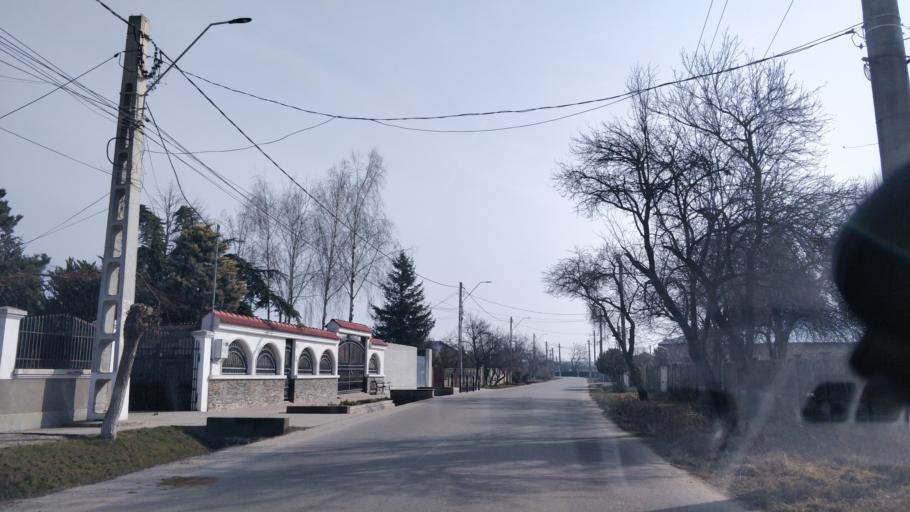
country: RO
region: Giurgiu
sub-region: Comuna Ulmi
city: Ulmi
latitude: 44.4819
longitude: 25.8055
